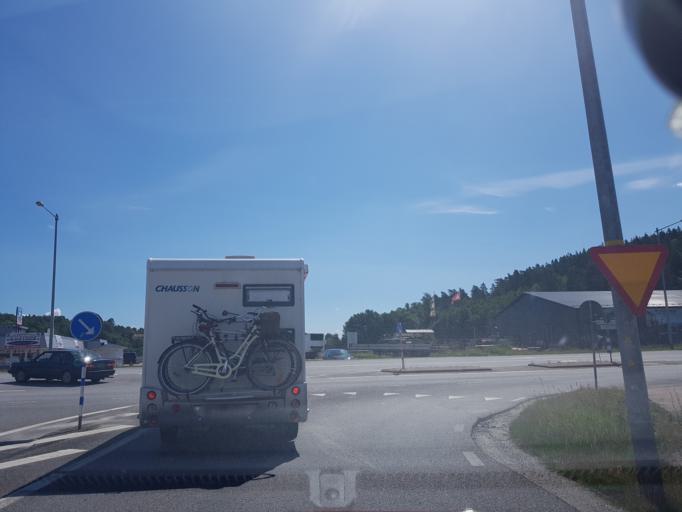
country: SE
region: Vaestra Goetaland
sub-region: Tjorns Kommun
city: Myggenas
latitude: 58.1247
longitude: 11.7213
